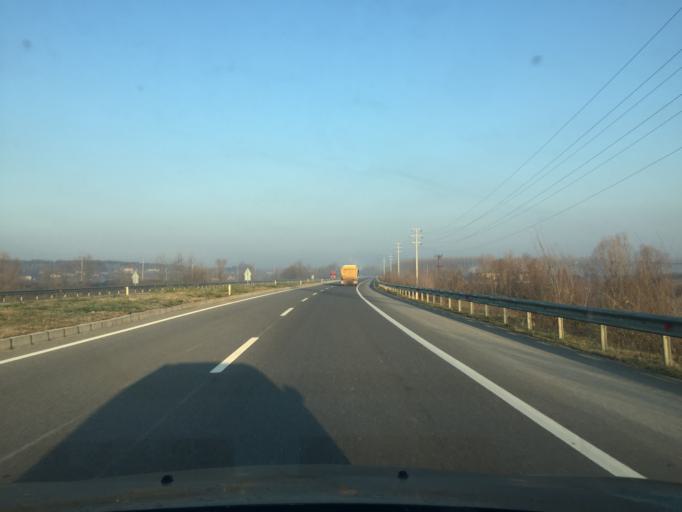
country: TR
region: Sakarya
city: Akyazi
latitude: 40.6499
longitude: 30.6044
